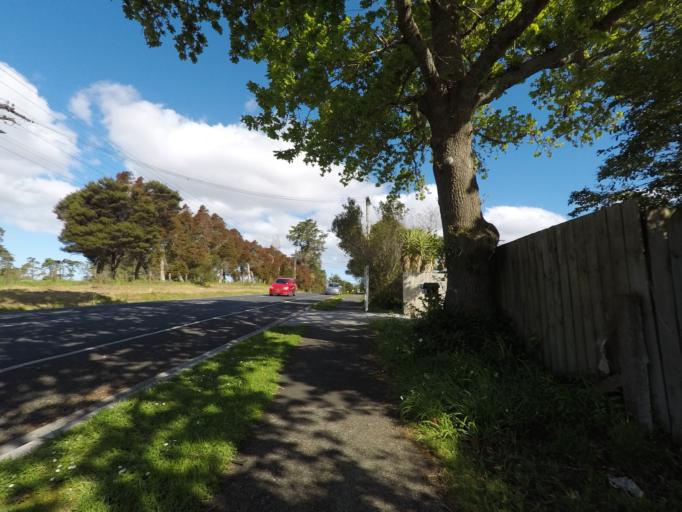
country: NZ
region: Auckland
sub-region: Auckland
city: Rosebank
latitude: -36.8557
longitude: 174.6036
